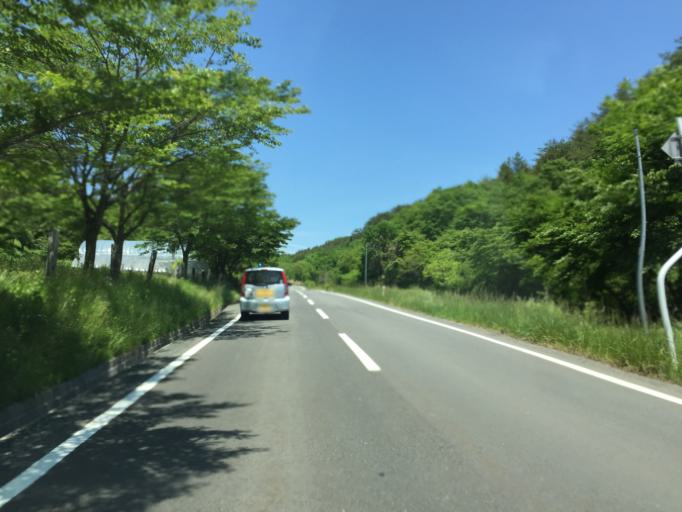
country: JP
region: Fukushima
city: Funehikimachi-funehiki
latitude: 37.5088
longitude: 140.7751
